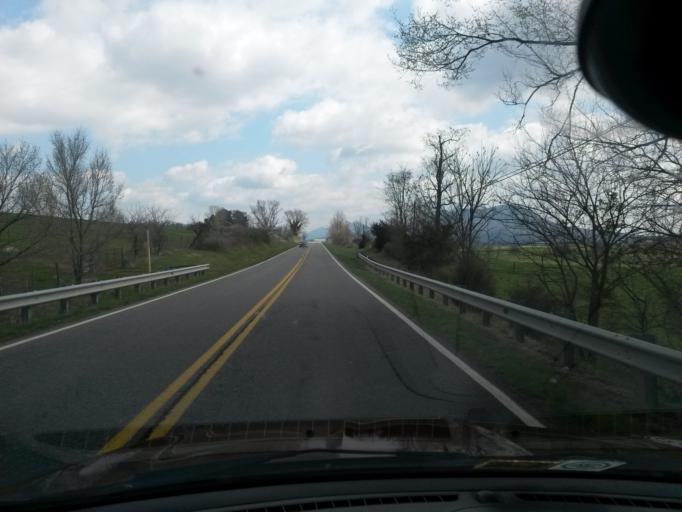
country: US
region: Virginia
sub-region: Rockingham County
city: Massanetta Springs
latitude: 38.3605
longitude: -78.8410
